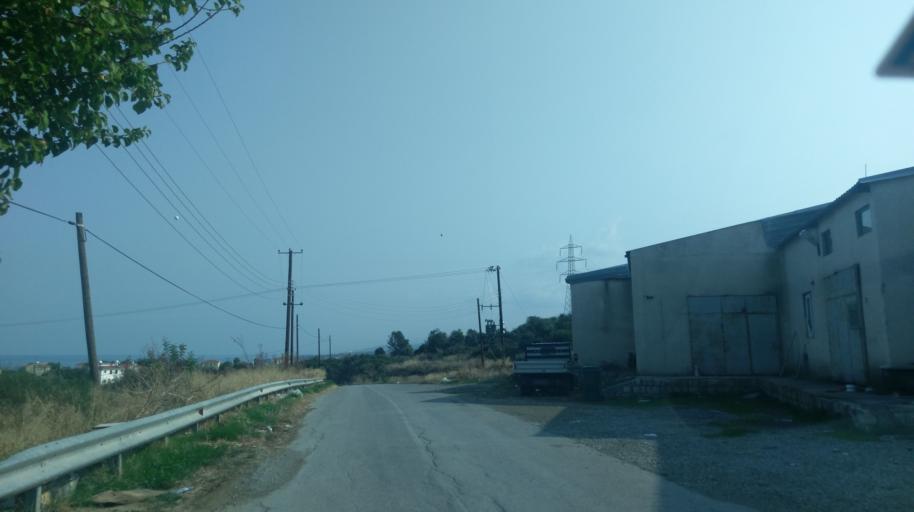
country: CY
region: Keryneia
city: Kyrenia
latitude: 35.3301
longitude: 33.4621
